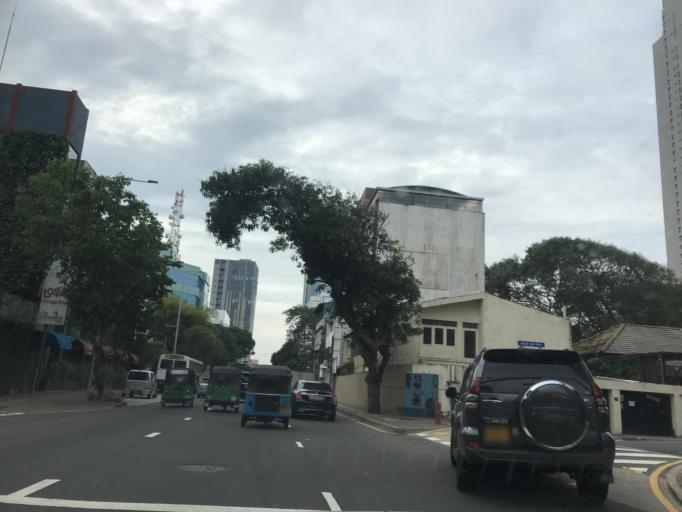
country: LK
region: Western
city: Colombo
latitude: 6.8980
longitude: 79.8561
